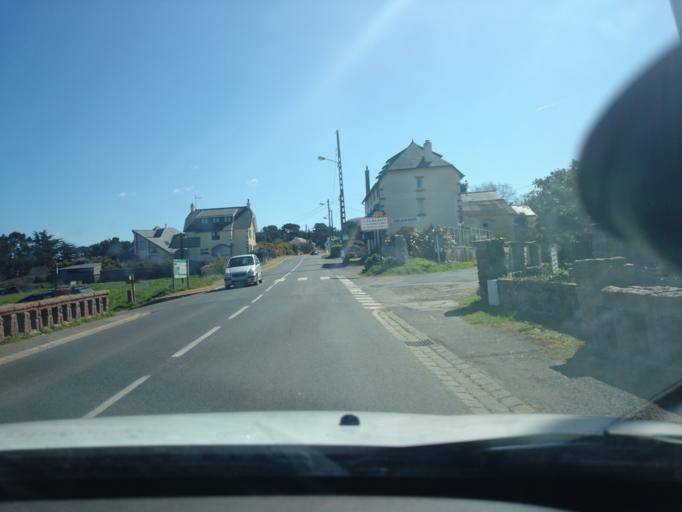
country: FR
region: Brittany
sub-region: Departement des Cotes-d'Armor
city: Tregastel
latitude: 48.8254
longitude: -3.4896
